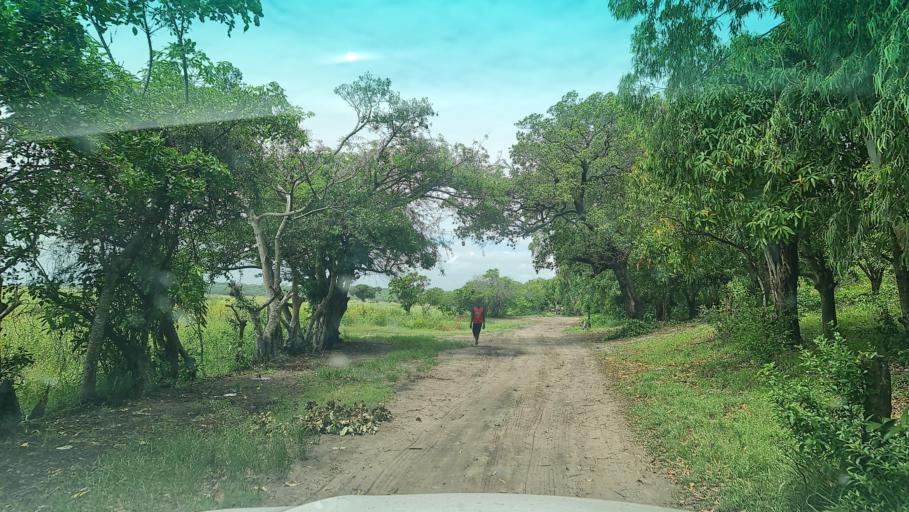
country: MZ
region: Maputo
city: Manhica
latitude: -25.5195
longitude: 32.8648
